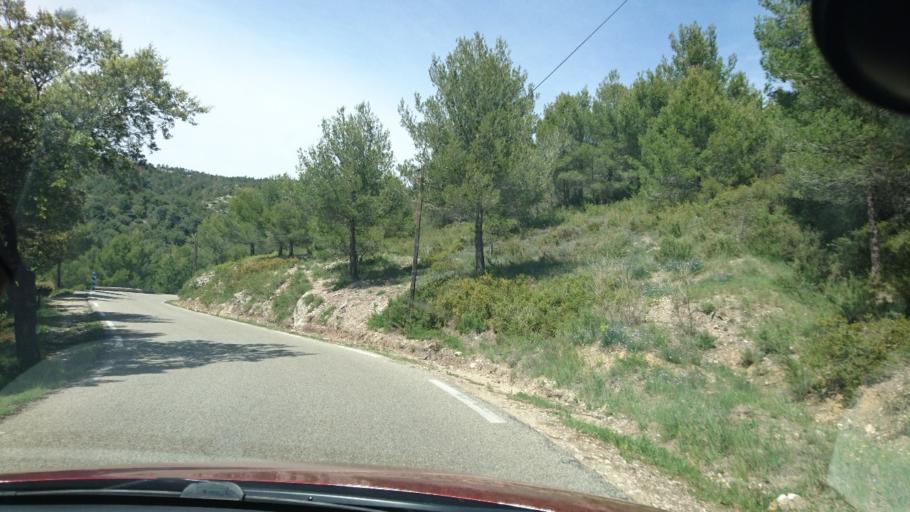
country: FR
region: Provence-Alpes-Cote d'Azur
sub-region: Departement du Vaucluse
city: Malaucene
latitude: 44.1409
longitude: 5.1422
